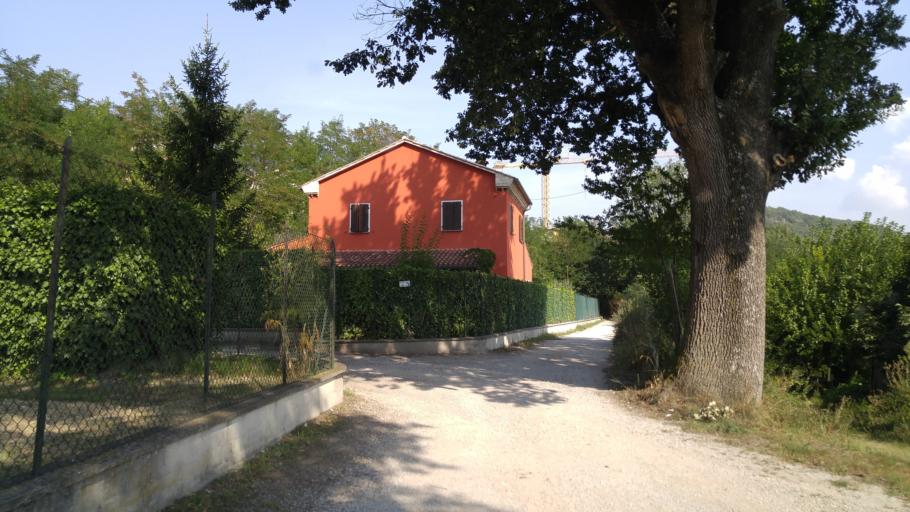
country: IT
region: The Marches
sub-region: Provincia di Pesaro e Urbino
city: Fermignano
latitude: 43.6957
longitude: 12.6658
